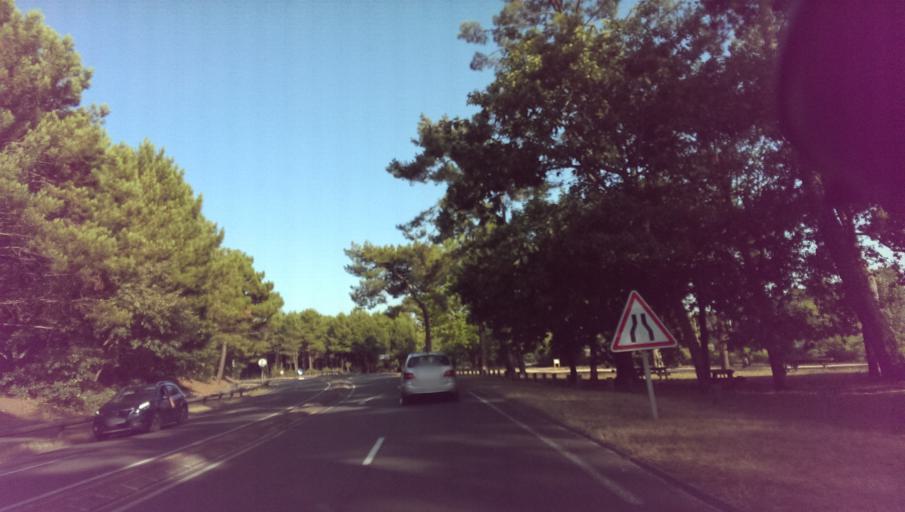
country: FR
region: Aquitaine
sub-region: Departement des Landes
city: Mimizan
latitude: 44.2109
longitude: -1.2752
